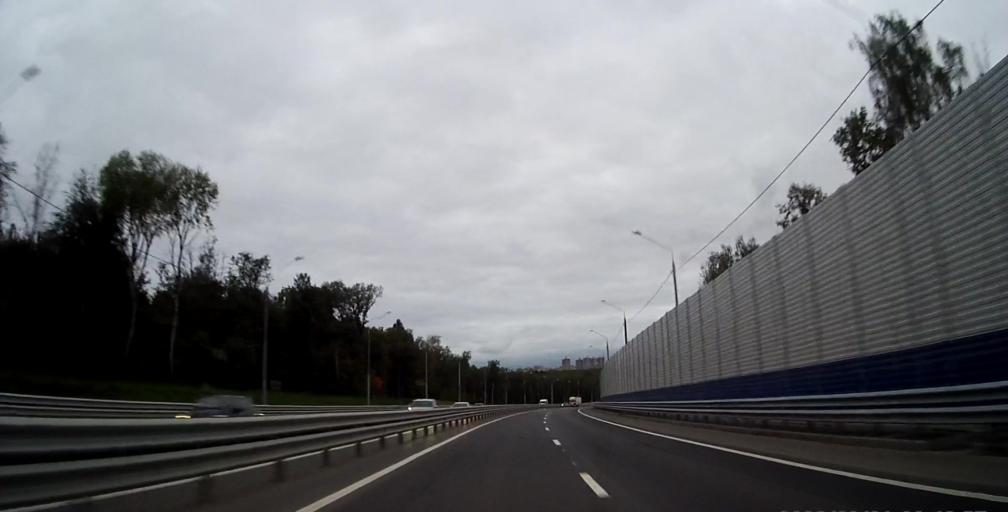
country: RU
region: Moskovskaya
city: Klimovsk
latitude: 55.3918
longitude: 37.5070
